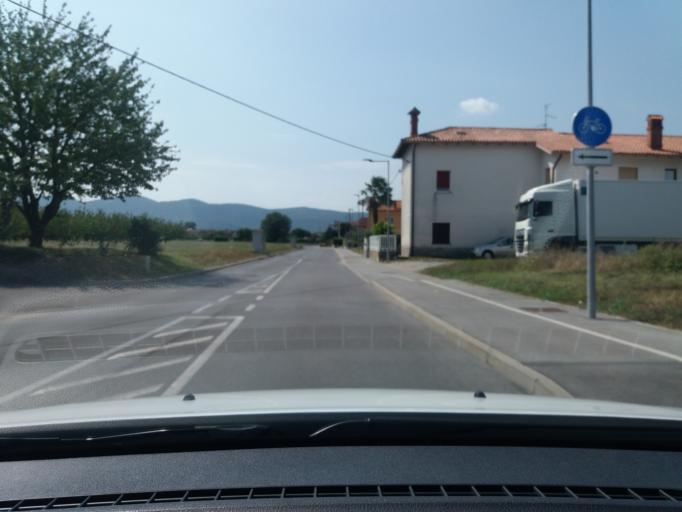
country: SI
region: Sempeter-Vrtojba
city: Sempeter pri Gorici
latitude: 45.9201
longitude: 13.6392
